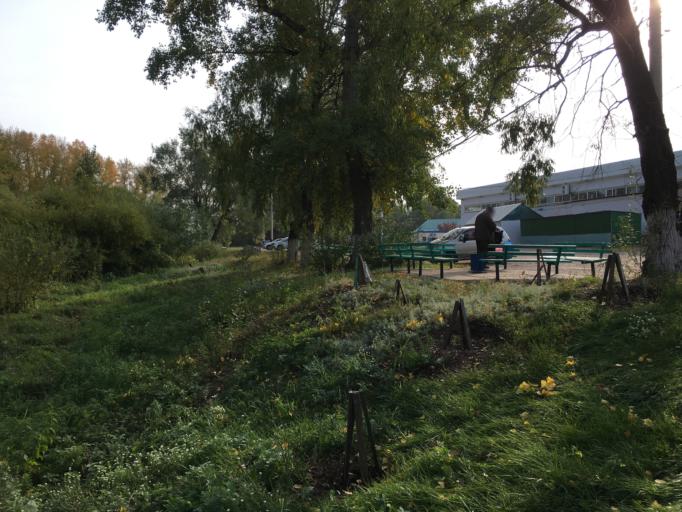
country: RU
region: Bashkortostan
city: Meleuz
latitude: 52.9580
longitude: 55.9204
